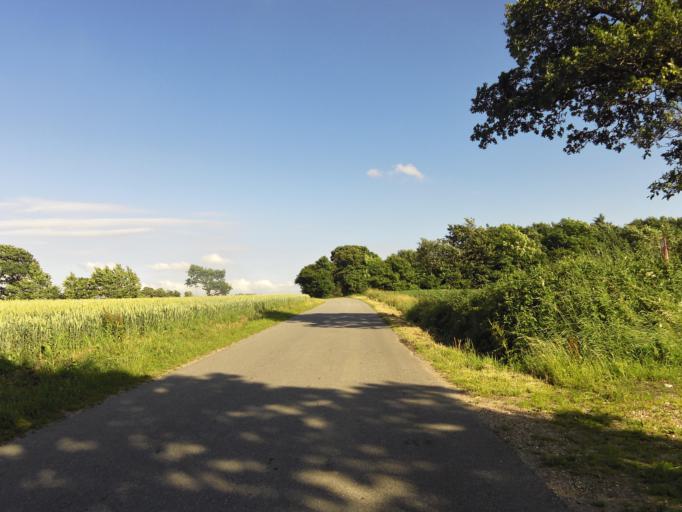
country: DK
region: South Denmark
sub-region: Vejen Kommune
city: Rodding
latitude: 55.3552
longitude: 9.0775
